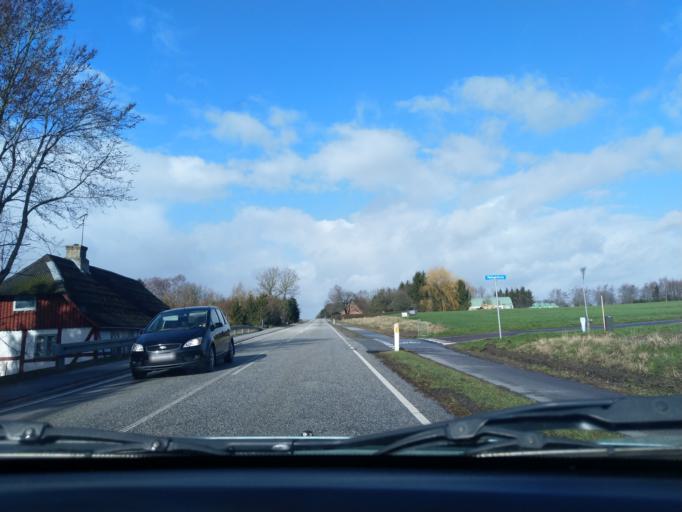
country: DK
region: Zealand
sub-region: Naestved Kommune
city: Naestved
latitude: 55.3062
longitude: 11.6883
